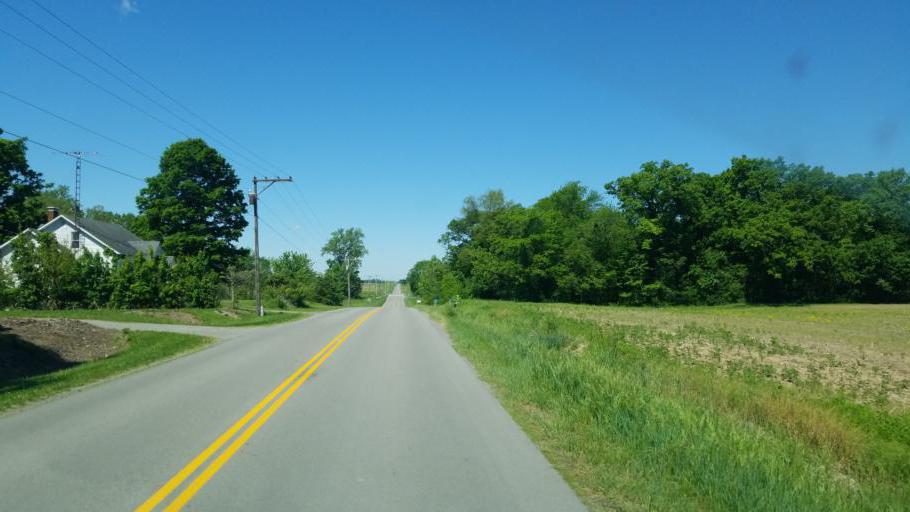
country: US
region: Ohio
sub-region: Logan County
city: Bellefontaine
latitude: 40.4284
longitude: -83.8109
